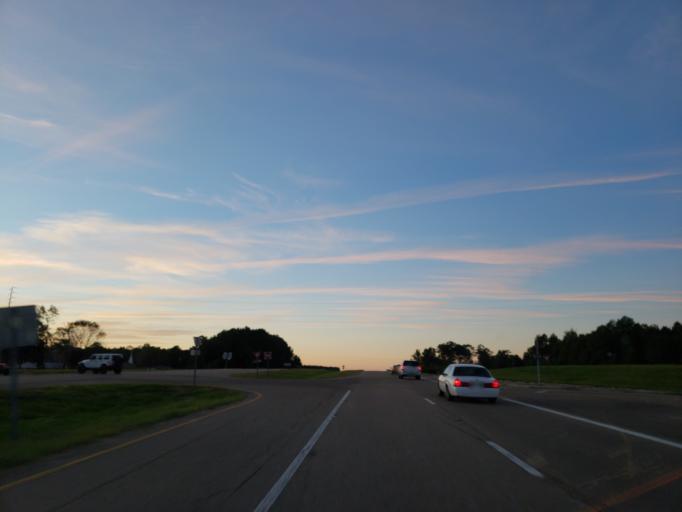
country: US
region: Mississippi
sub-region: Wayne County
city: Waynesboro
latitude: 31.7000
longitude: -88.6200
